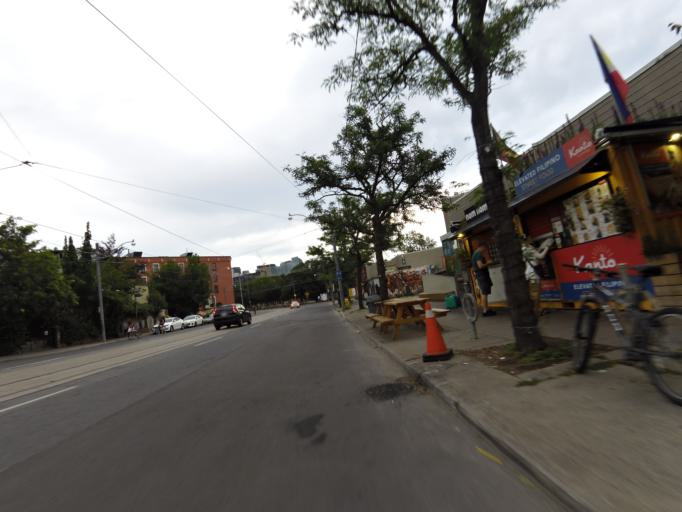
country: CA
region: Ontario
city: Toronto
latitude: 43.6521
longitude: -79.4049
